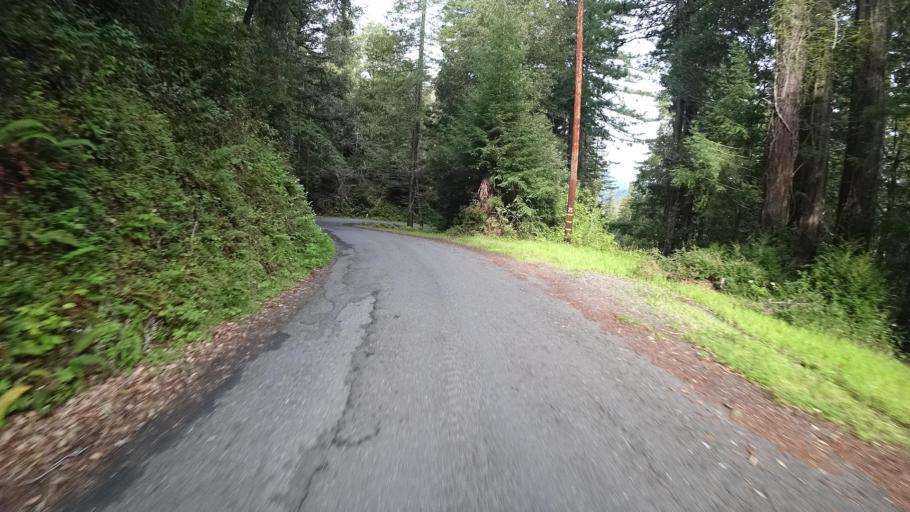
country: US
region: California
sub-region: Humboldt County
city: Redway
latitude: 40.3398
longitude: -123.8712
